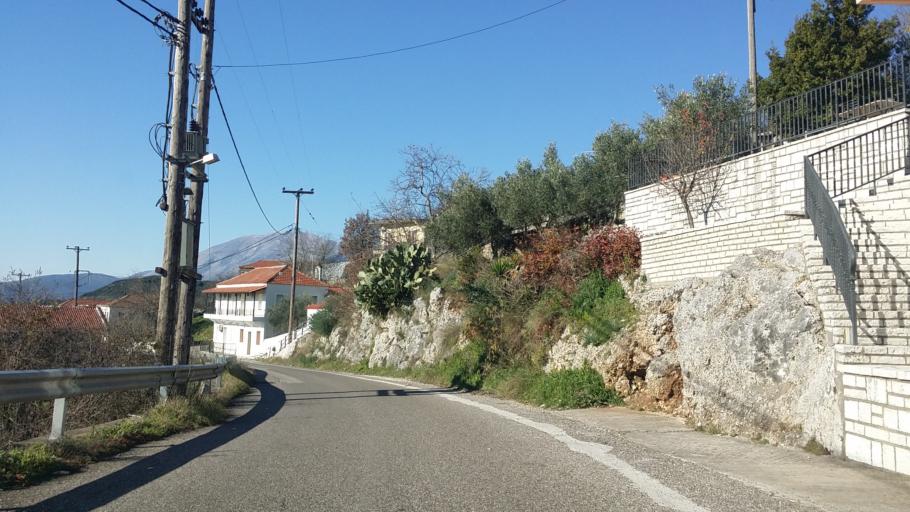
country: GR
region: West Greece
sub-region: Nomos Aitolias kai Akarnanias
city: Fitiai
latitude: 38.7088
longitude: 21.1735
